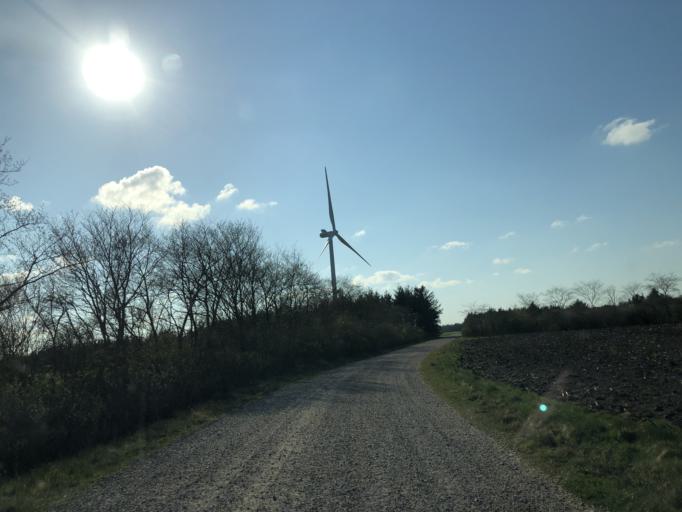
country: DK
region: Central Jutland
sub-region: Holstebro Kommune
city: Ulfborg
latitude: 56.3680
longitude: 8.3238
